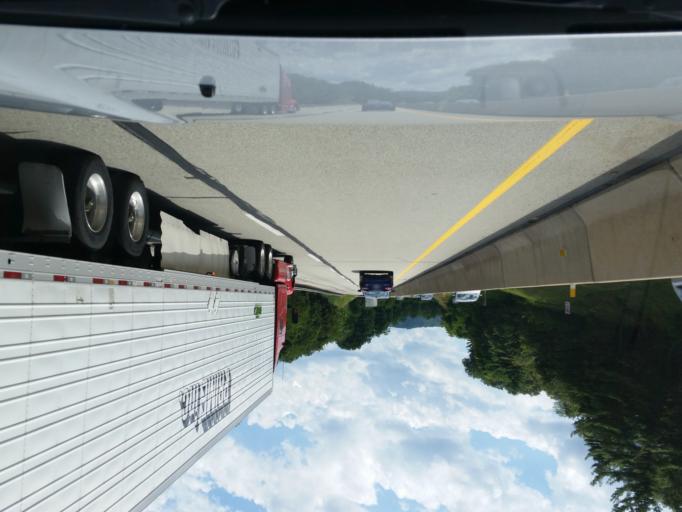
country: US
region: Pennsylvania
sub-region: Fulton County
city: McConnellsburg
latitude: 40.0761
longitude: -77.8890
